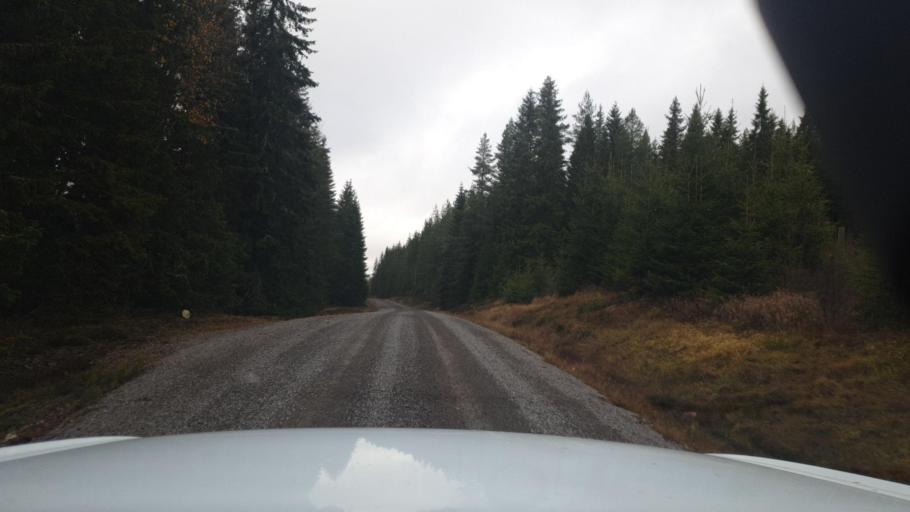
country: SE
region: Vaermland
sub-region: Eda Kommun
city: Charlottenberg
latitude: 60.0918
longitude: 12.6152
